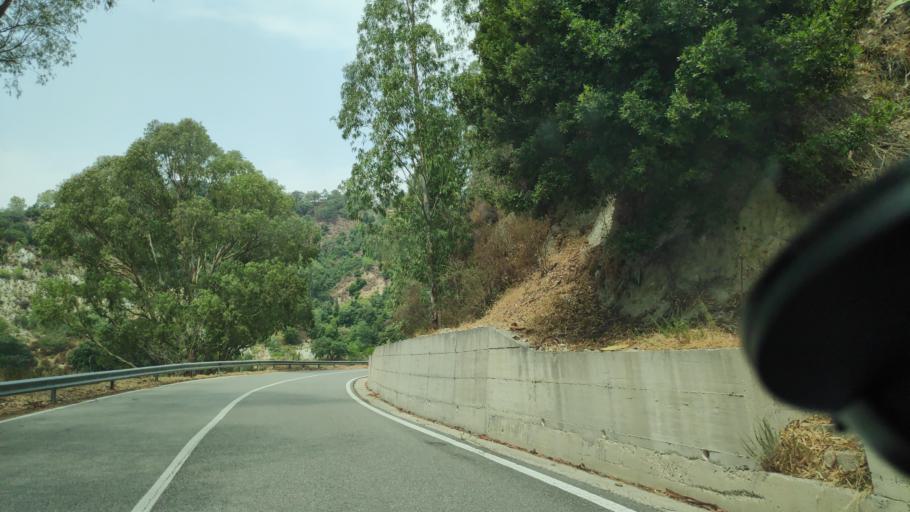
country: IT
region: Calabria
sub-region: Provincia di Catanzaro
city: Sant'Andrea Apostolo dello Ionio
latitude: 38.6420
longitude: 16.5150
